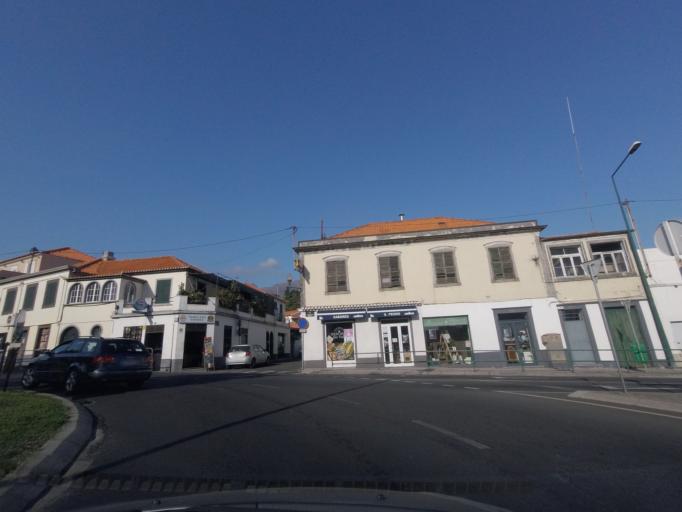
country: PT
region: Madeira
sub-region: Funchal
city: Funchal
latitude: 32.6492
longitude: -16.9238
